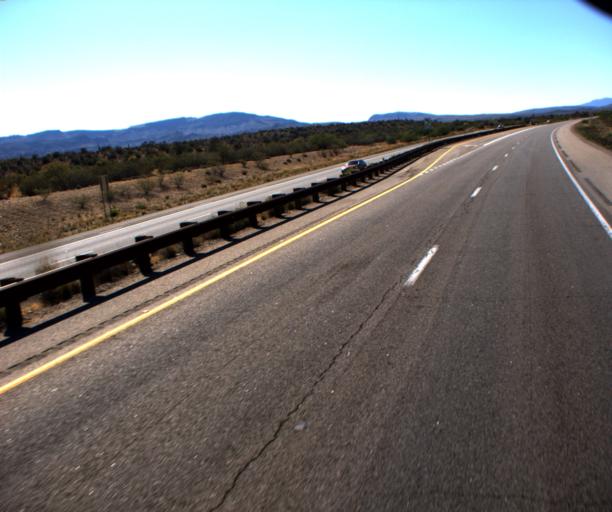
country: US
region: Arizona
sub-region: Yavapai County
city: Bagdad
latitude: 34.6618
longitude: -113.5799
